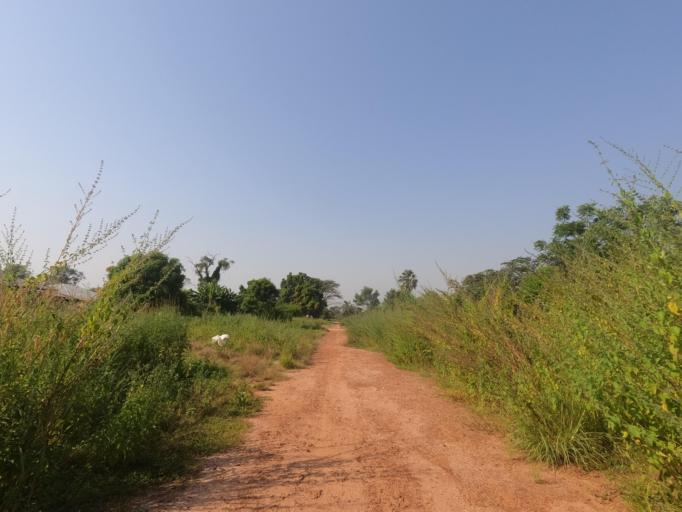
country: SN
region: Sedhiou
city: Sedhiou
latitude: 12.4442
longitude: -15.7390
